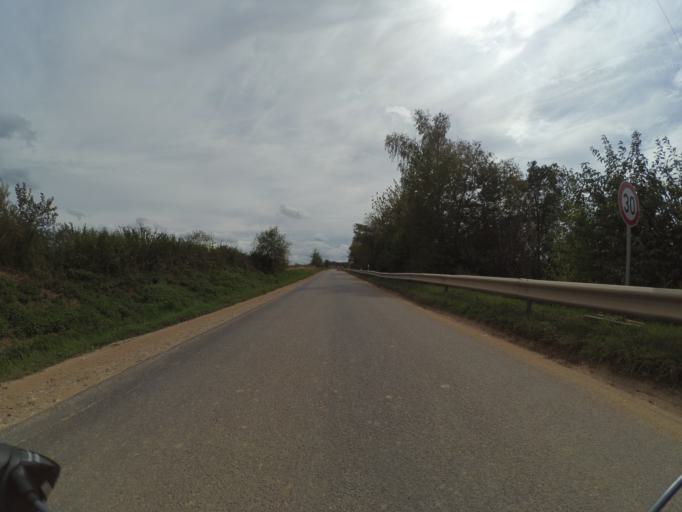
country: DE
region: Rheinland-Pfalz
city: Dodenburg
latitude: 49.9242
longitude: 6.7749
